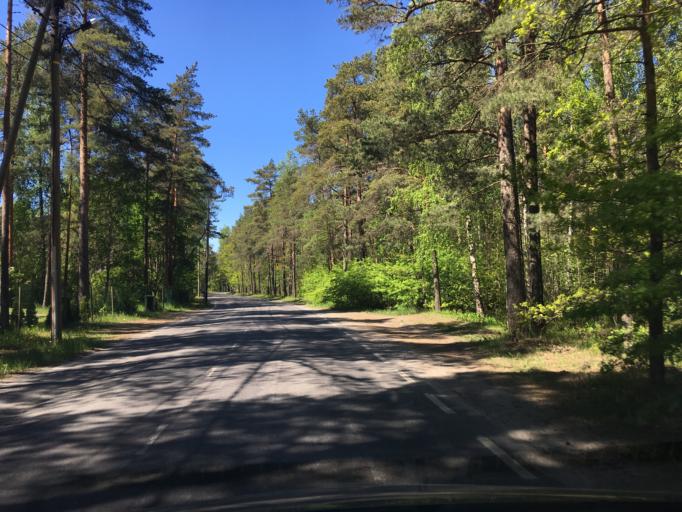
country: EE
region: Harju
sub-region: Saue vald
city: Laagri
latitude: 59.3853
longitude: 24.6498
